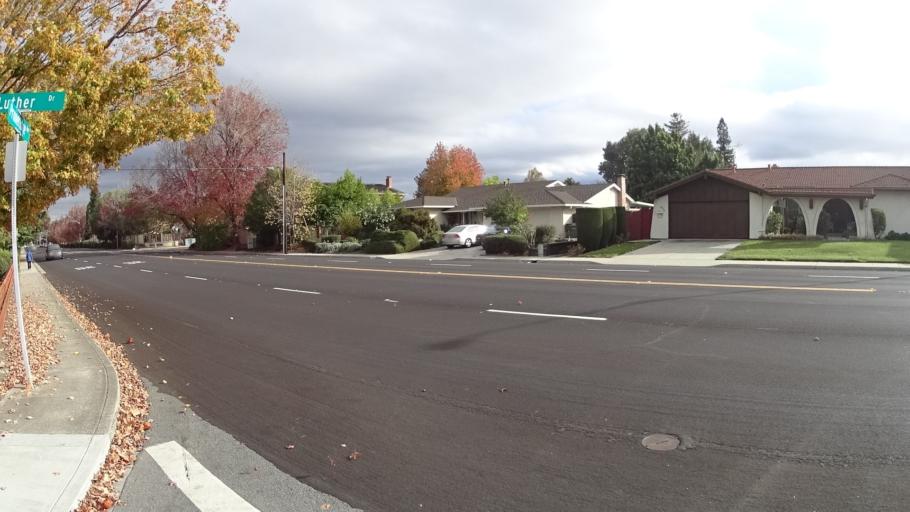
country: US
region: California
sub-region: Santa Clara County
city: Santa Clara
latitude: 37.3301
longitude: -121.9722
